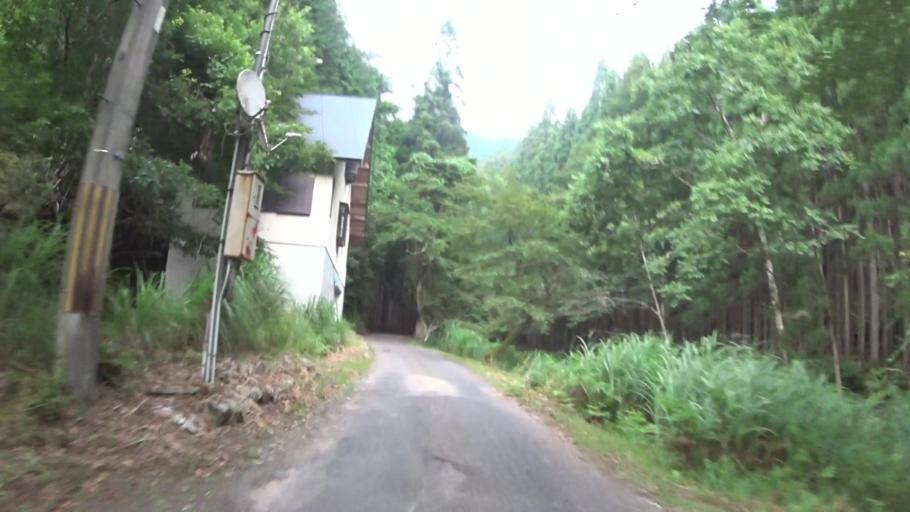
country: JP
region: Shiga Prefecture
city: Kitahama
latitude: 35.2633
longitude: 135.7759
